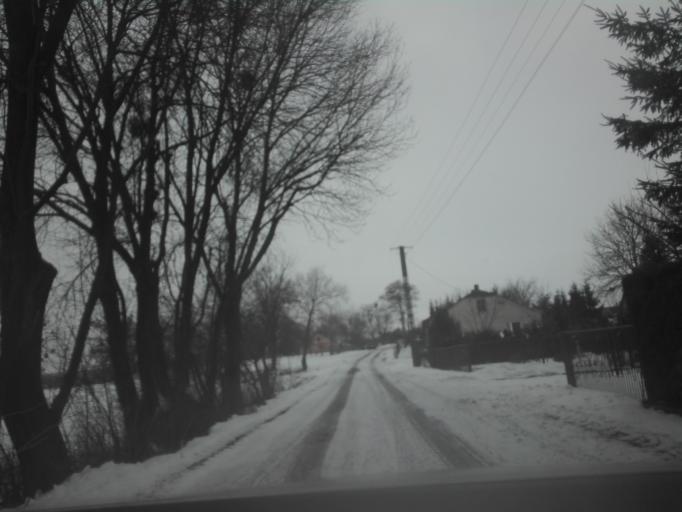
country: PL
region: Lublin Voivodeship
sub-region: Powiat hrubieszowski
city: Horodlo
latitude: 50.8408
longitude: 24.0143
